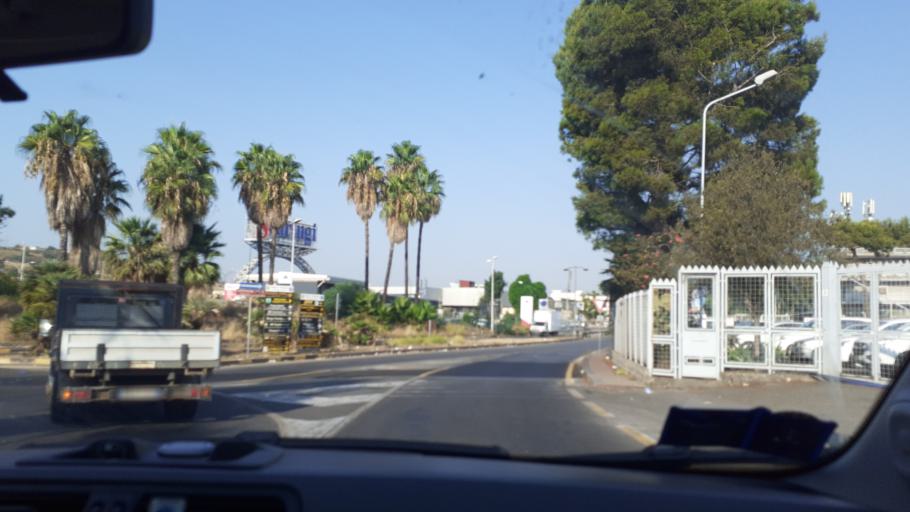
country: IT
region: Sicily
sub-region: Catania
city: Misterbianco
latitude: 37.5115
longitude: 15.0353
